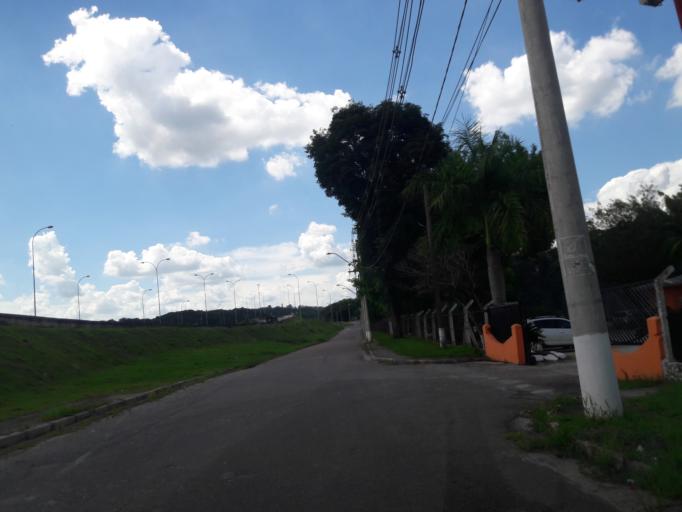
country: BR
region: Sao Paulo
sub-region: Campo Limpo Paulista
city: Campo Limpo Paulista
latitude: -23.2050
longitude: -46.7942
